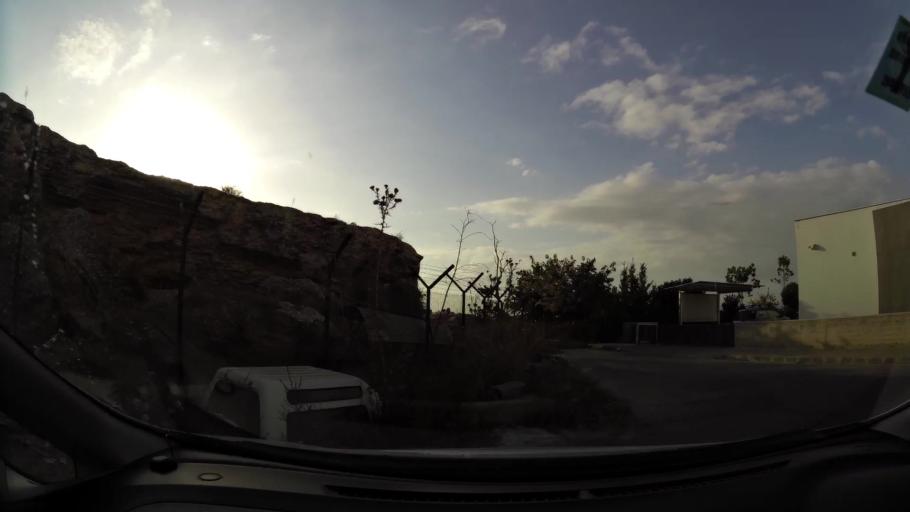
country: CY
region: Lefkosia
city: Nicosia
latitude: 35.1634
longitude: 33.3906
